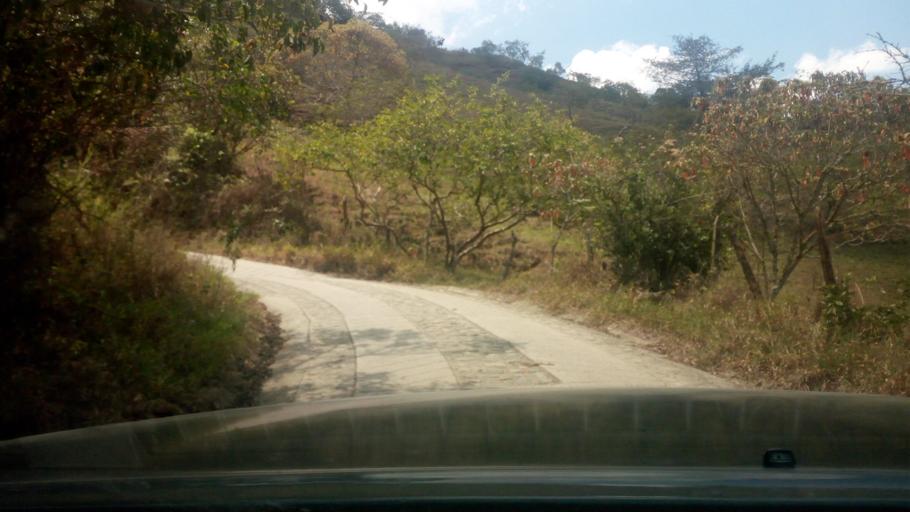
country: CO
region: Boyaca
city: Somondoco
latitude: 4.9874
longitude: -73.4483
